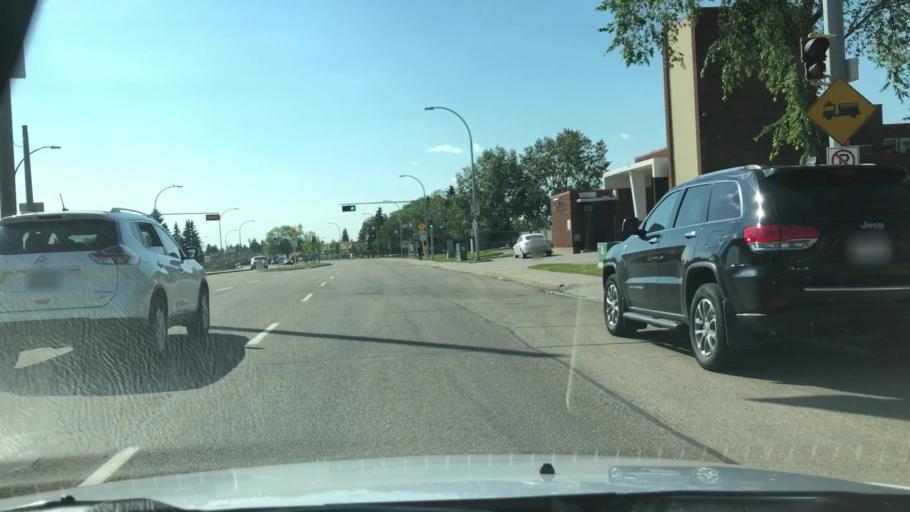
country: CA
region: Alberta
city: Edmonton
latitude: 53.6064
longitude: -113.4532
